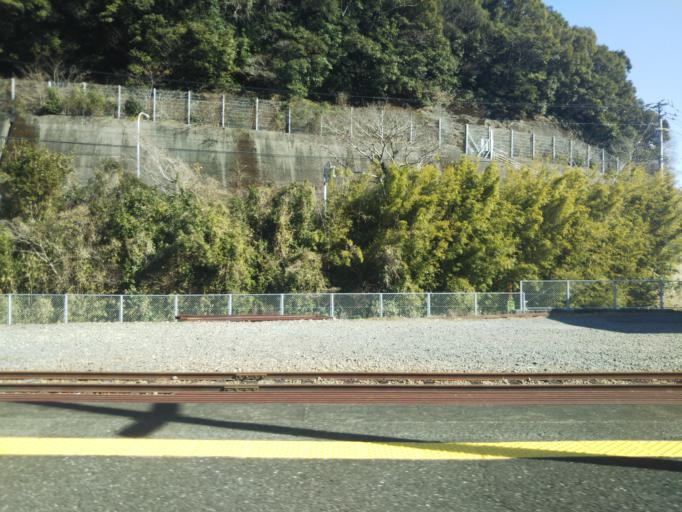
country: JP
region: Kochi
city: Nakamura
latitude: 33.0815
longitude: 133.1015
